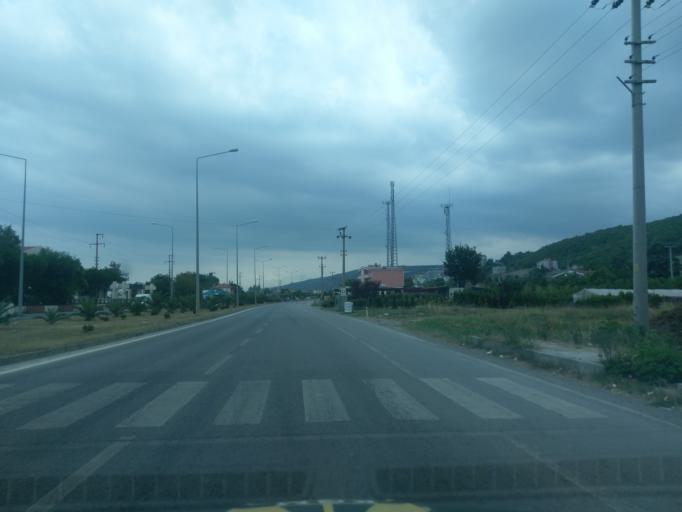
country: TR
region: Samsun
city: Taflan
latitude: 41.4150
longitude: 36.1730
